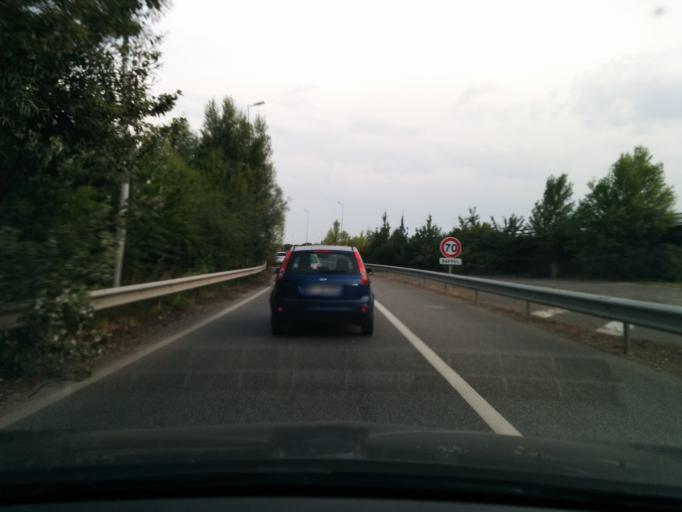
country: FR
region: Midi-Pyrenees
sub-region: Departement de la Haute-Garonne
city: Ramonville-Saint-Agne
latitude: 43.5547
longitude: 1.4966
